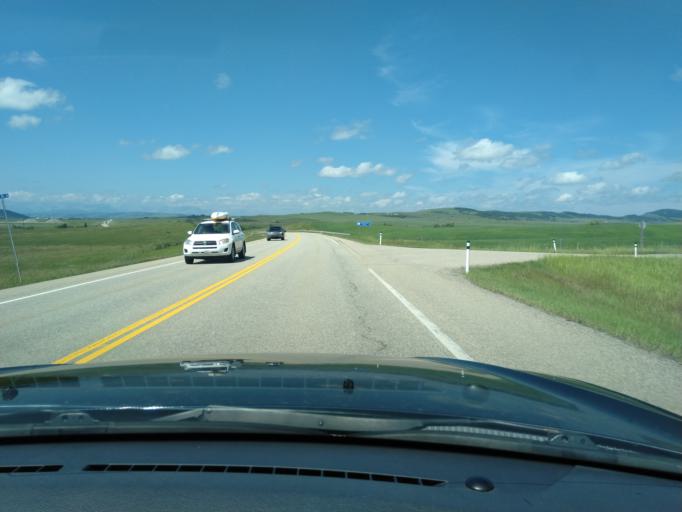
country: CA
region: Alberta
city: Cochrane
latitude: 51.2274
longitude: -114.5726
